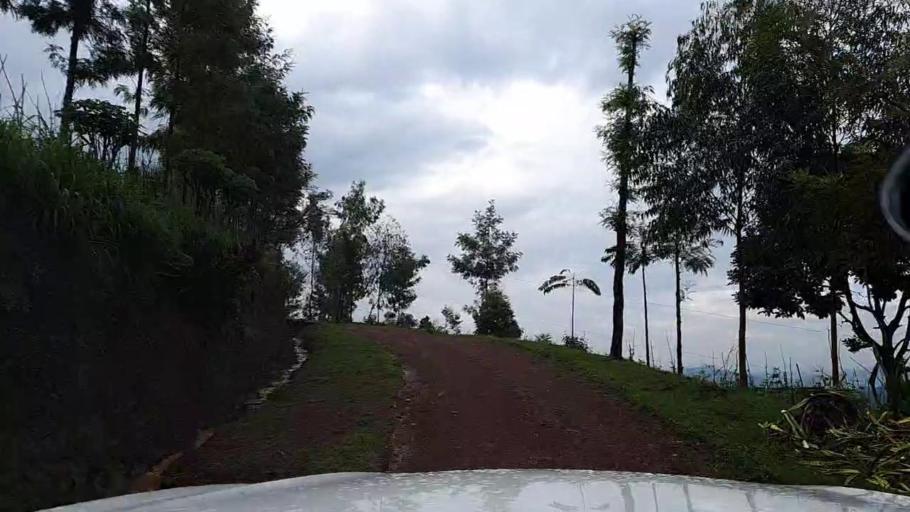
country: RW
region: Northern Province
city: Byumba
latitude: -1.7203
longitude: 29.9087
